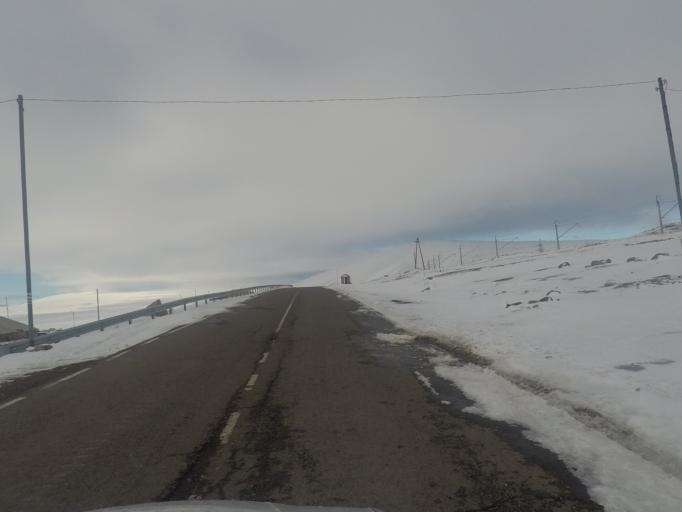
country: GE
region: Kvemo Kartli
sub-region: Tsalka
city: Tsalka
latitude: 41.4531
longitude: 43.8537
